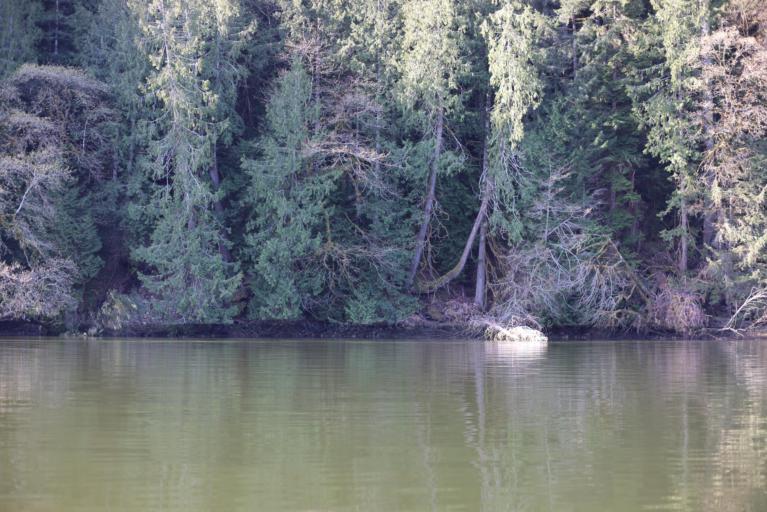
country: CA
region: British Columbia
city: Langford
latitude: 48.5588
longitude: -123.4718
